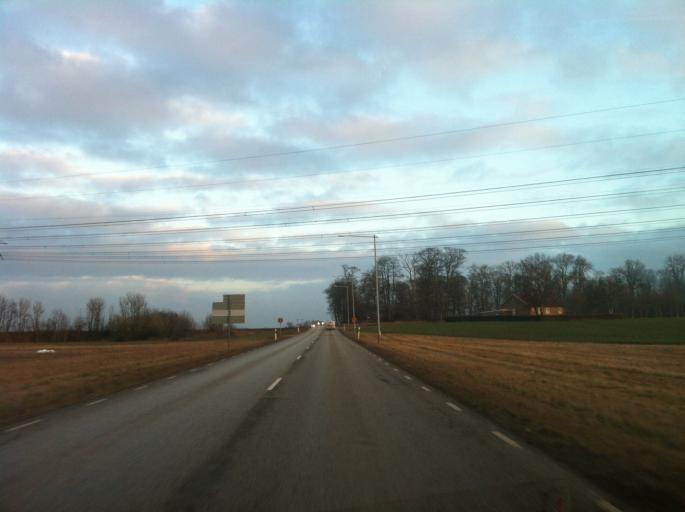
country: SE
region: Skane
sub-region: Kavlinge Kommun
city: Kaevlinge
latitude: 55.8107
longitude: 13.0583
